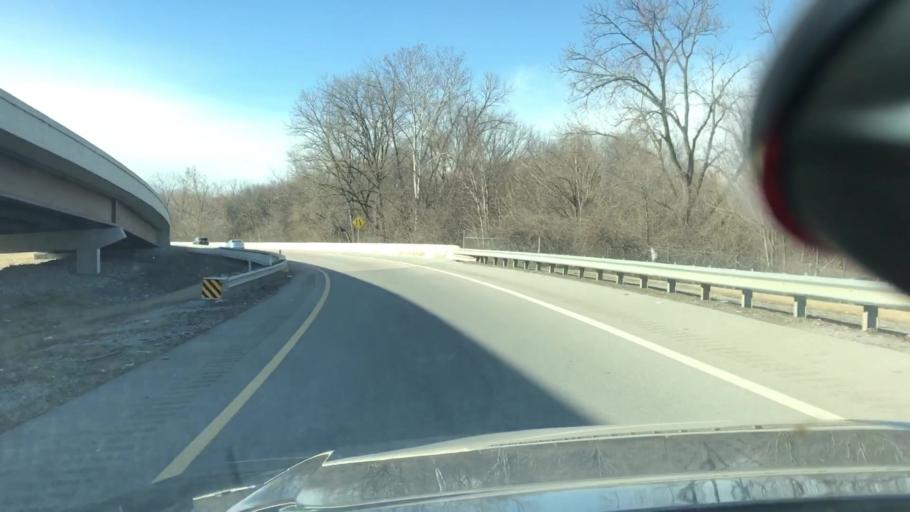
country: US
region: Tennessee
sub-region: Davidson County
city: Belle Meade
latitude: 36.1567
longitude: -86.8584
